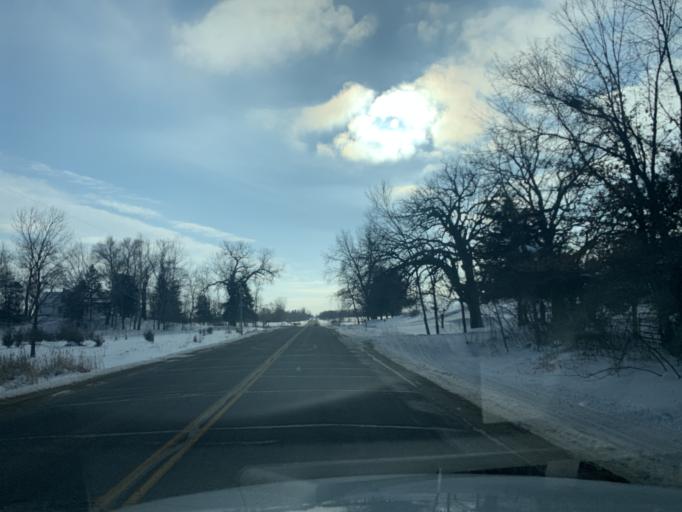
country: US
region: Minnesota
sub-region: Wright County
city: Buffalo
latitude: 45.1991
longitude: -93.8271
